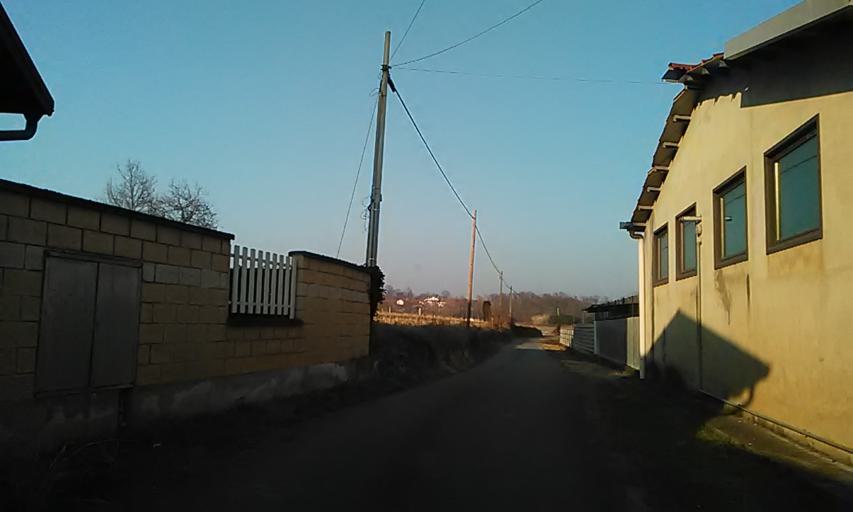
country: IT
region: Piedmont
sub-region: Provincia di Biella
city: Cavaglia
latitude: 45.4111
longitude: 8.1017
